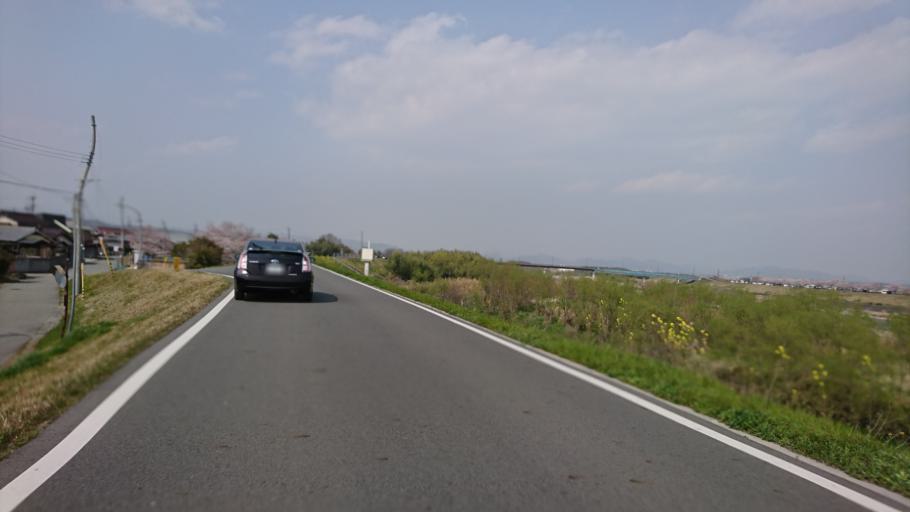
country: JP
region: Hyogo
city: Ono
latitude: 34.8729
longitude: 134.9233
